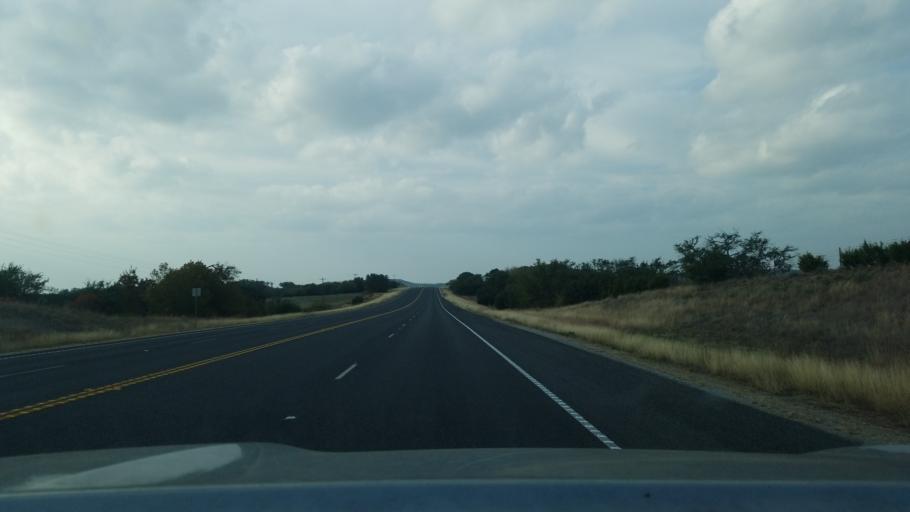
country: US
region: Texas
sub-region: Mills County
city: Goldthwaite
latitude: 31.3769
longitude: -98.5305
